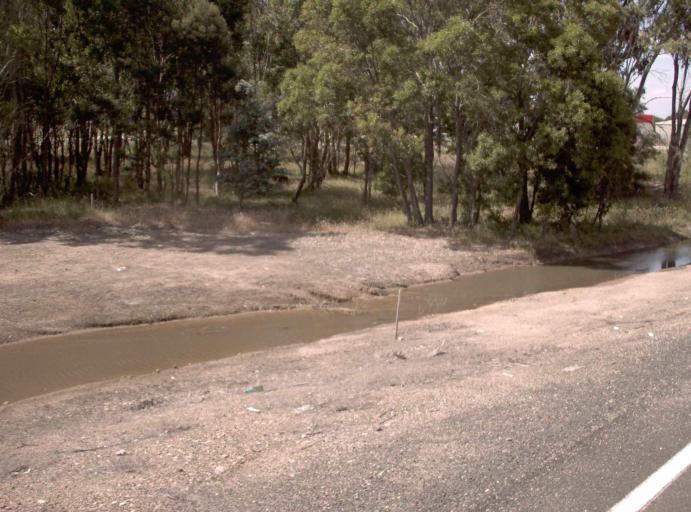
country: AU
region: Victoria
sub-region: East Gippsland
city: Bairnsdale
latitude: -37.8441
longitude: 147.5877
